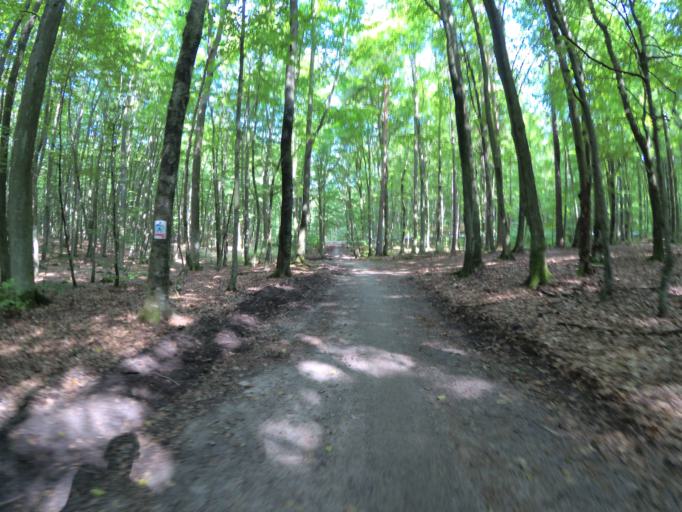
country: PL
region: Pomeranian Voivodeship
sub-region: Gdynia
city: Wielki Kack
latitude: 54.5019
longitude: 18.4921
